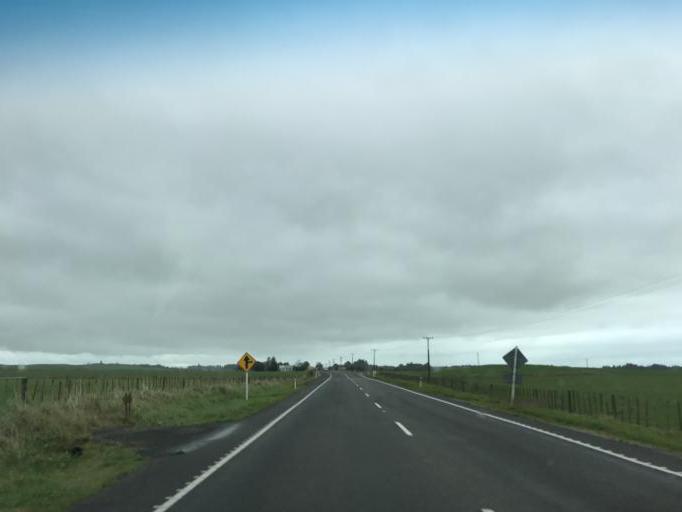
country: NZ
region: Manawatu-Wanganui
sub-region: Wanganui District
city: Wanganui
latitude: -39.8149
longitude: 174.8256
